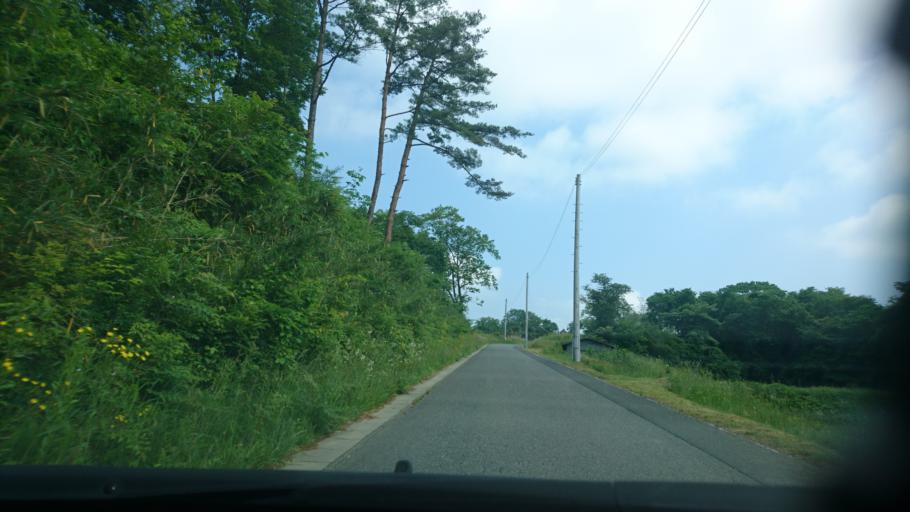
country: JP
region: Iwate
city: Ichinoseki
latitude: 38.8983
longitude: 141.2405
